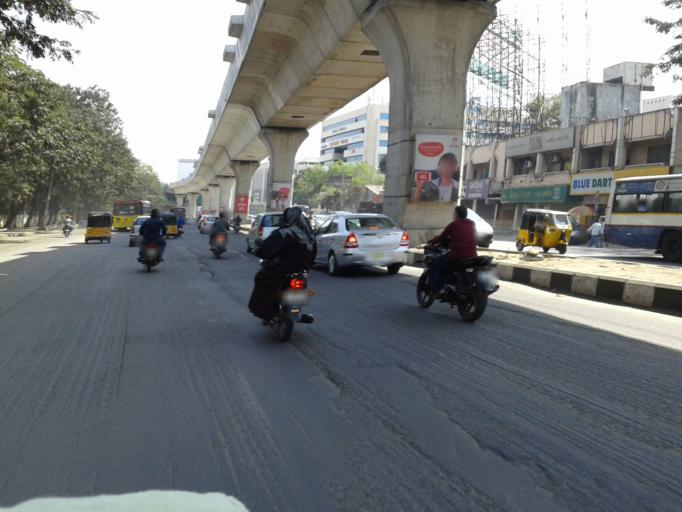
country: IN
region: Telangana
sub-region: Hyderabad
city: Malkajgiri
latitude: 17.4440
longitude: 78.4728
